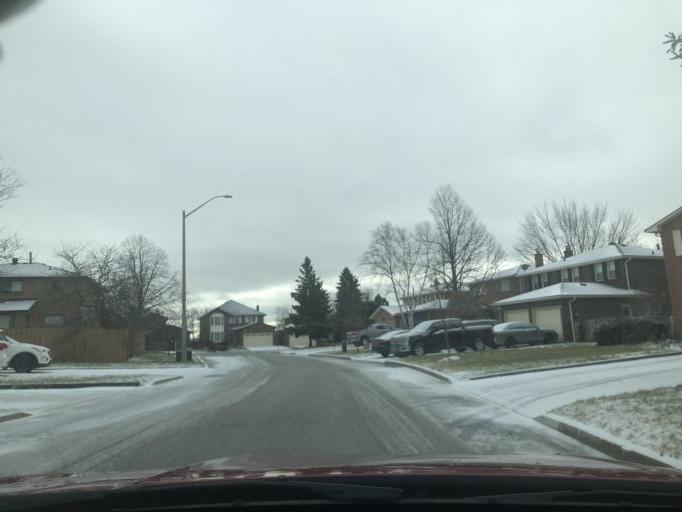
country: CA
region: Ontario
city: Markham
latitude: 43.8707
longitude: -79.2425
